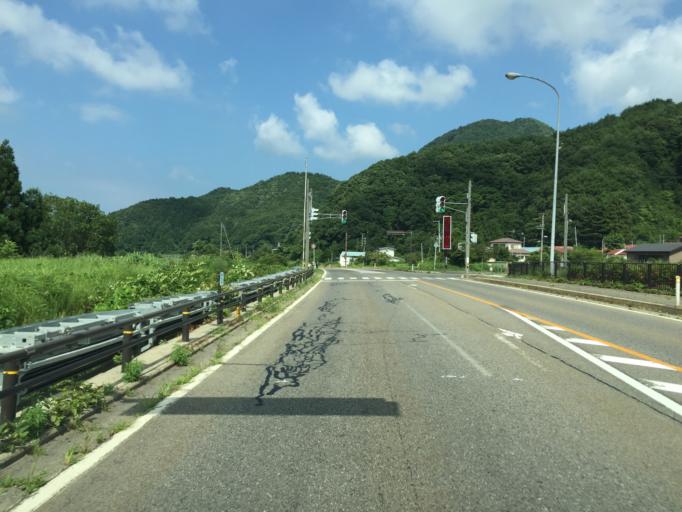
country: JP
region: Fukushima
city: Inawashiro
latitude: 37.4841
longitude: 140.1906
